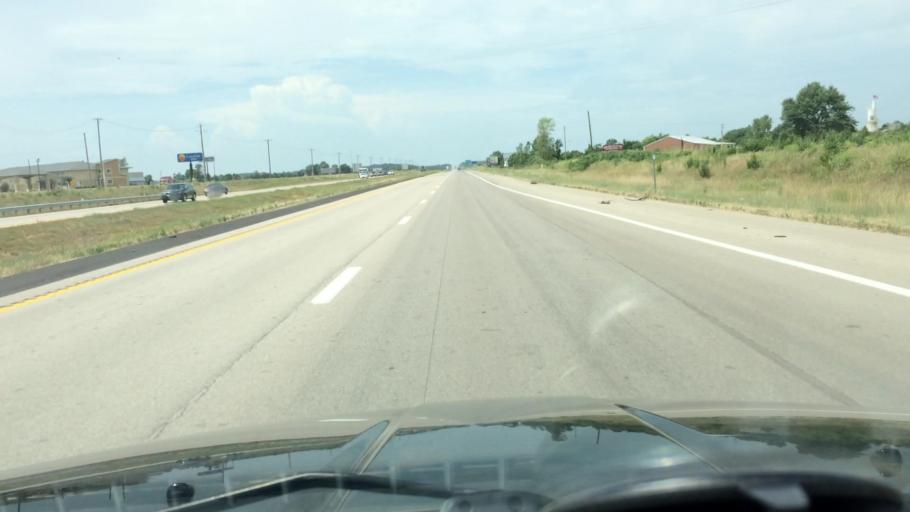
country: US
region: Missouri
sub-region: Polk County
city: Bolivar
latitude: 37.5973
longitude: -93.4358
